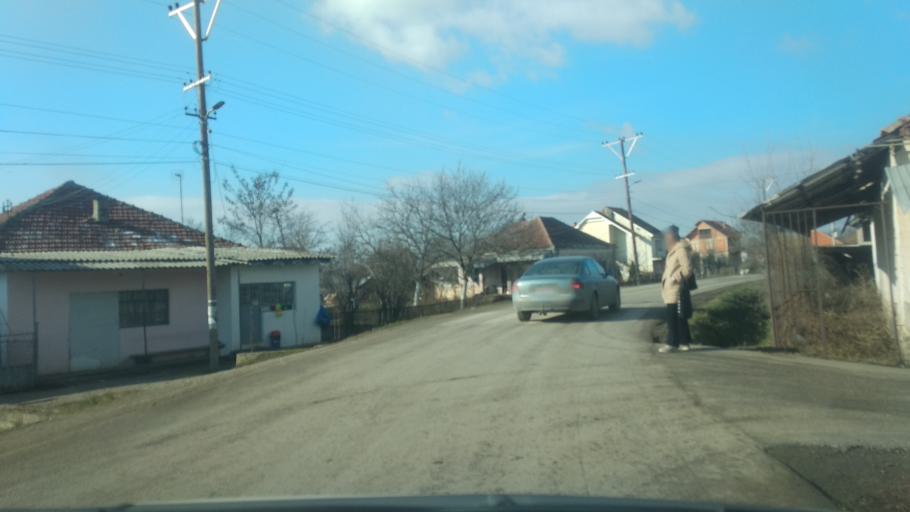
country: XK
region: Pristina
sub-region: Lipjan
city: Lipljan
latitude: 42.5644
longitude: 21.1655
